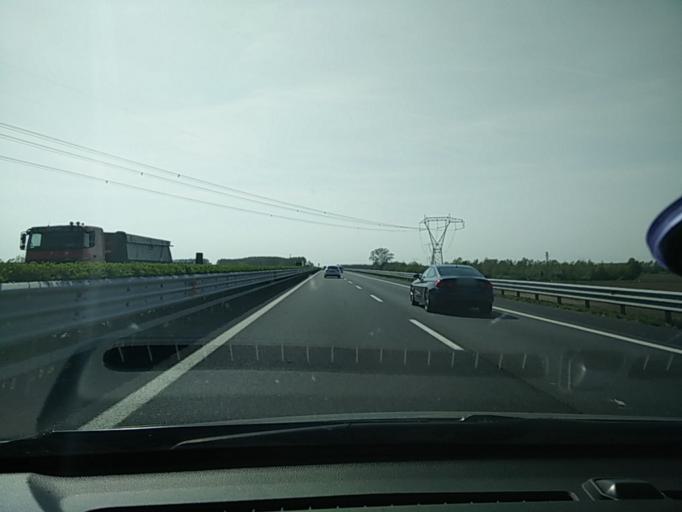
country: IT
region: Friuli Venezia Giulia
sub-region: Provincia di Udine
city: Pocenia
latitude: 45.8288
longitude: 13.0840
